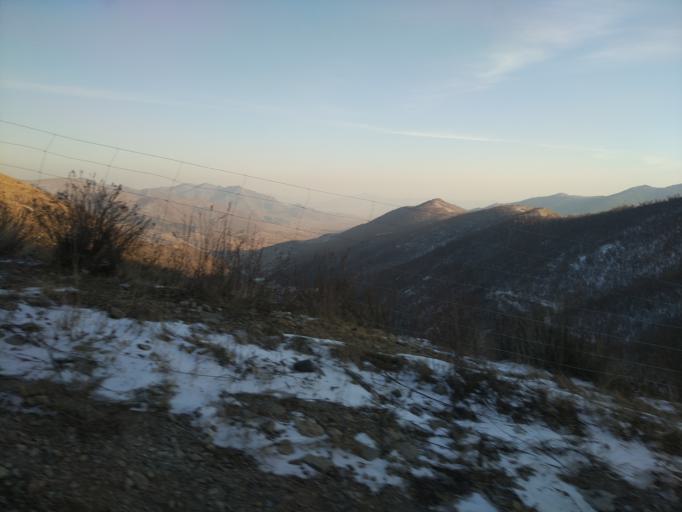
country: CN
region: Hebei
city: Xiwanzi
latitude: 40.8730
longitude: 115.4528
